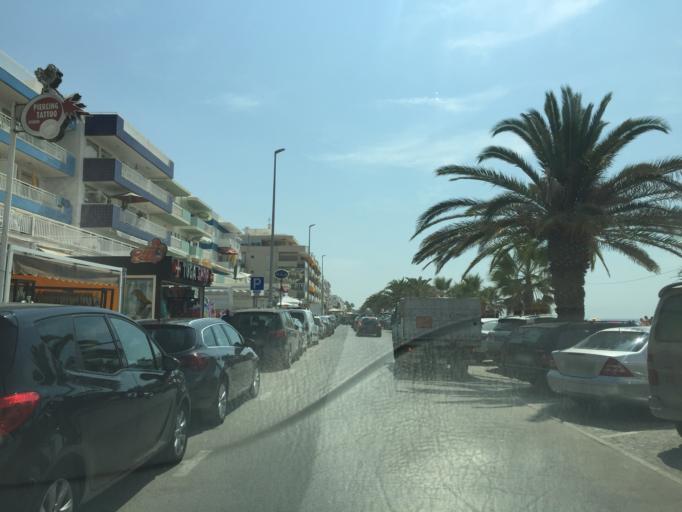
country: PT
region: Faro
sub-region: Loule
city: Quarteira
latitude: 37.0669
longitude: -8.1020
